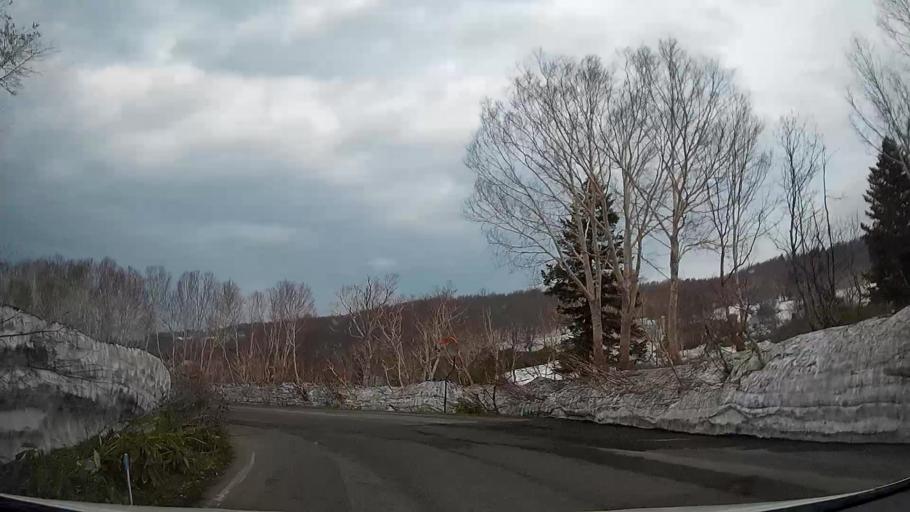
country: JP
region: Aomori
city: Aomori Shi
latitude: 40.6466
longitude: 140.8575
